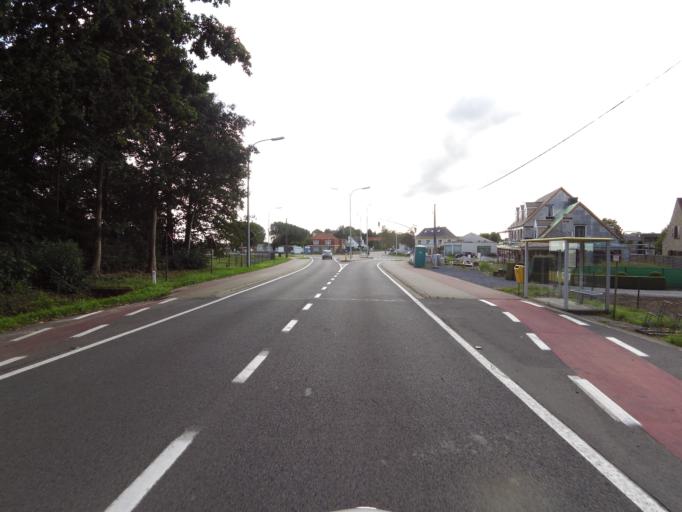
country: BE
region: Flanders
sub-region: Provincie West-Vlaanderen
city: Oostkamp
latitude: 51.1019
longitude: 3.2255
